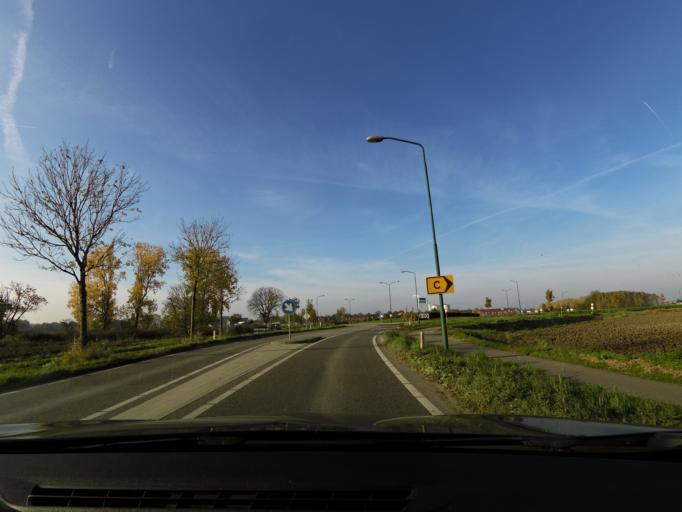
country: NL
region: North Brabant
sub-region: Gemeente Moerdijk
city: Klundert
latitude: 51.6370
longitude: 4.6184
